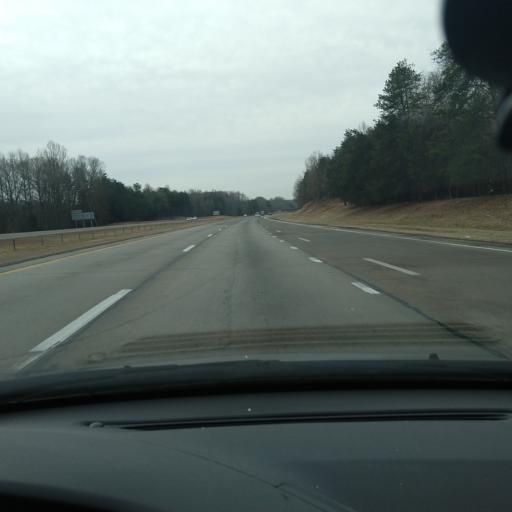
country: US
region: North Carolina
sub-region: Davidson County
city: Midway
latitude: 35.9650
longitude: -80.2301
